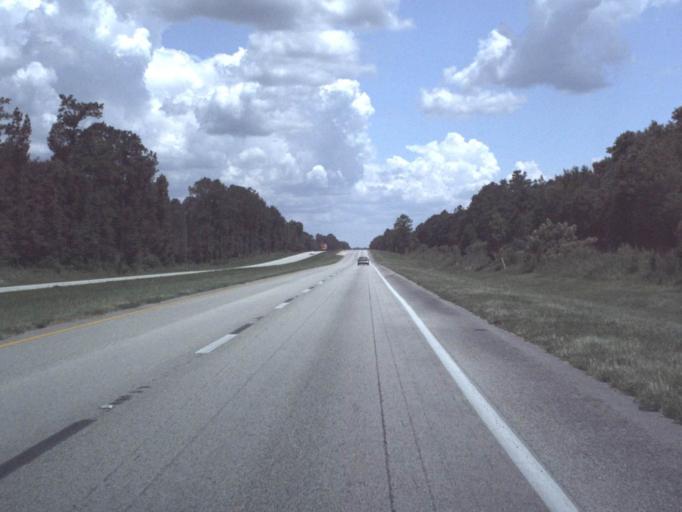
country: US
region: Florida
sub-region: Alachua County
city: Hawthorne
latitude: 29.6456
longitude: -82.1086
